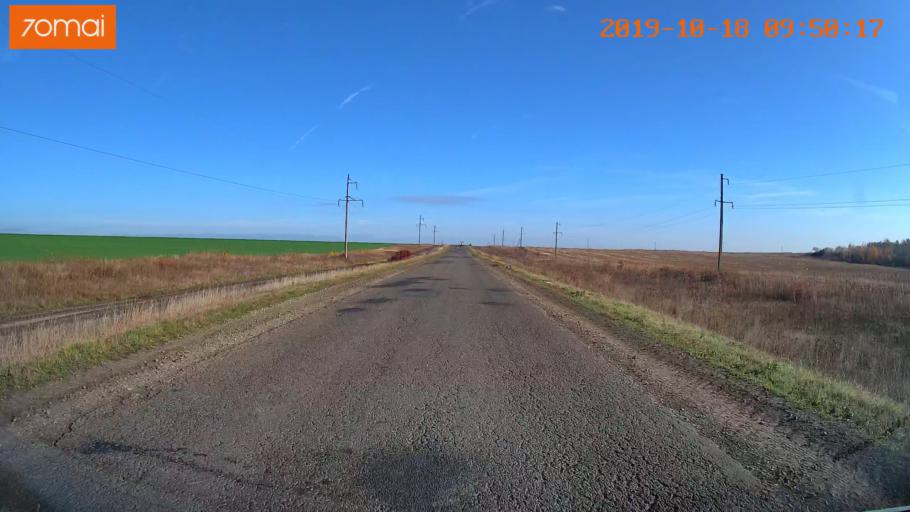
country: RU
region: Tula
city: Kazachka
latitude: 53.3272
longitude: 38.2755
